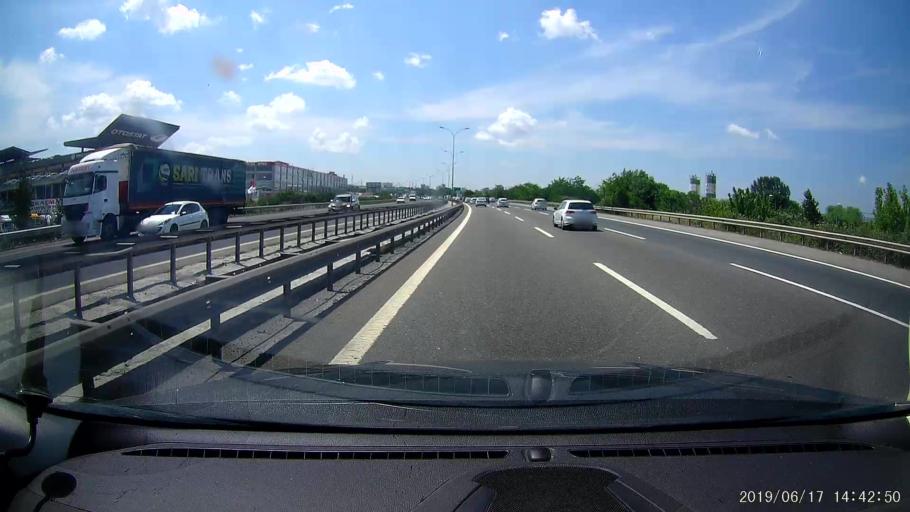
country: TR
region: Istanbul
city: Samandira
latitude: 40.9816
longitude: 29.2158
